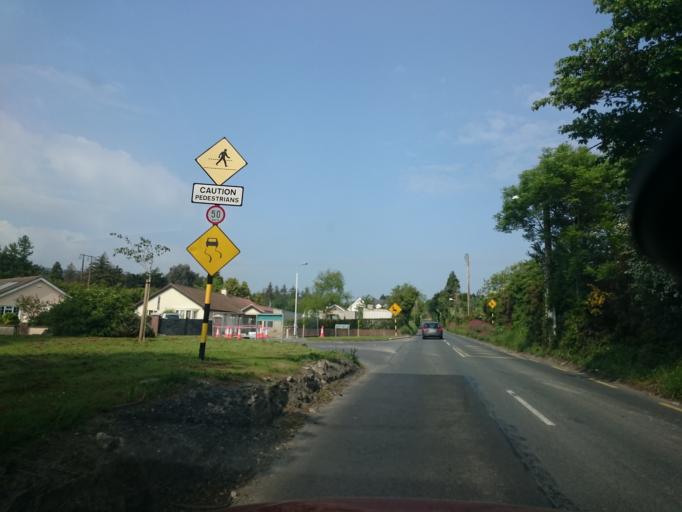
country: IE
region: Leinster
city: Sandyford
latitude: 53.2653
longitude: -6.2304
